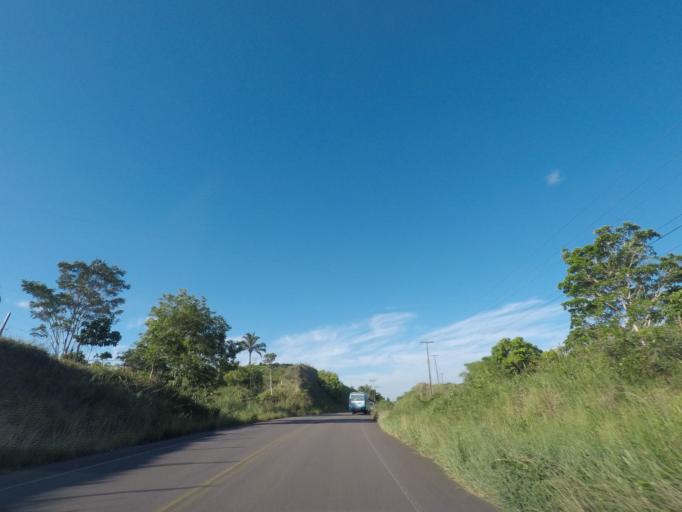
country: BR
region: Bahia
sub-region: Nazare
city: Nazare
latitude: -13.0592
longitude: -39.0072
